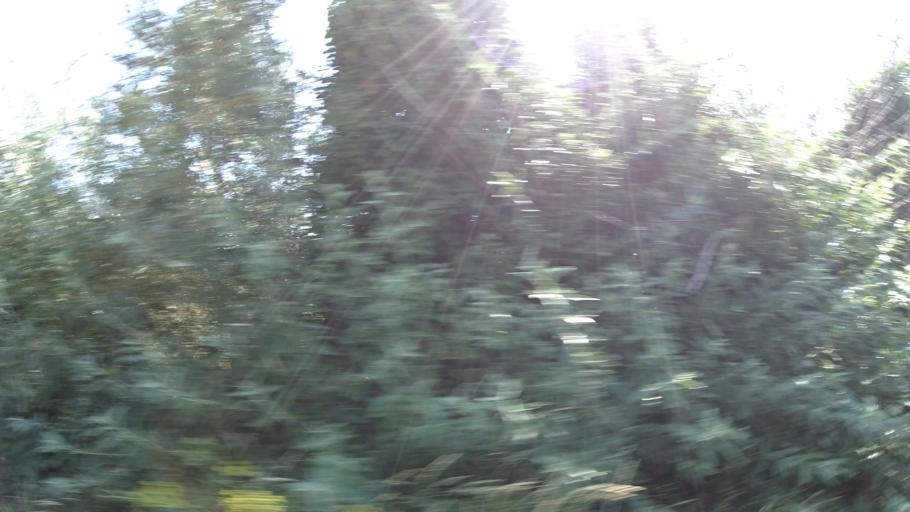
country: FR
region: Languedoc-Roussillon
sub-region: Departement des Pyrenees-Orientales
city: Sainte-Marie-Plage
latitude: 42.7380
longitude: 3.0250
